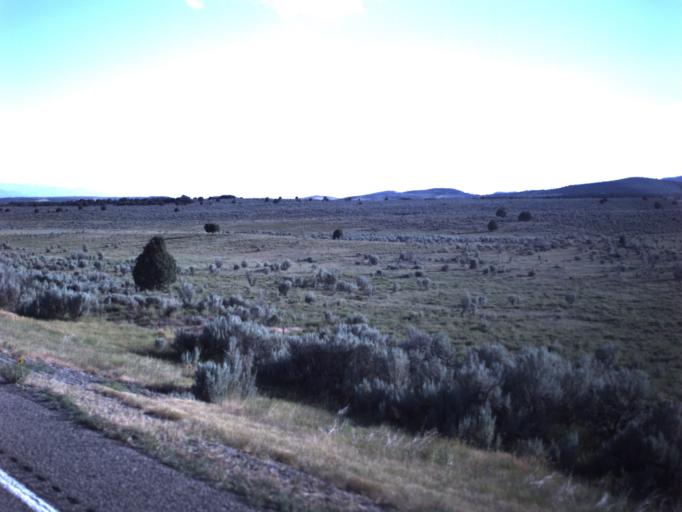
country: US
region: Utah
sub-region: Sanpete County
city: Fairview
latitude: 39.6856
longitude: -111.4589
